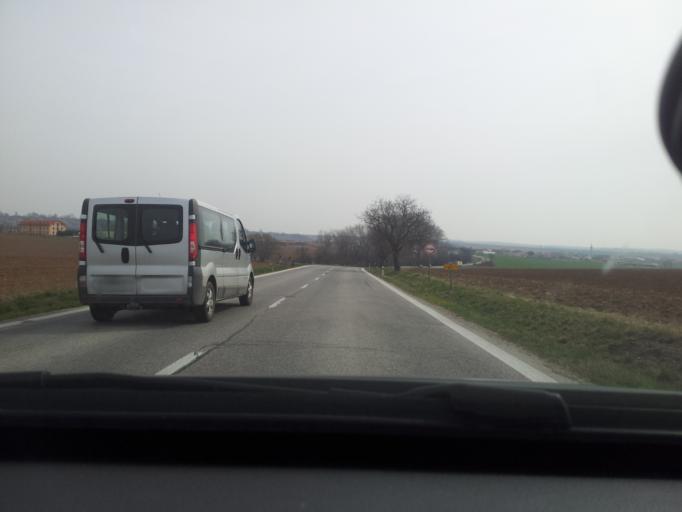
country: SK
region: Nitriansky
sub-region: Okres Nitra
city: Nitra
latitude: 48.2996
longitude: 18.1665
